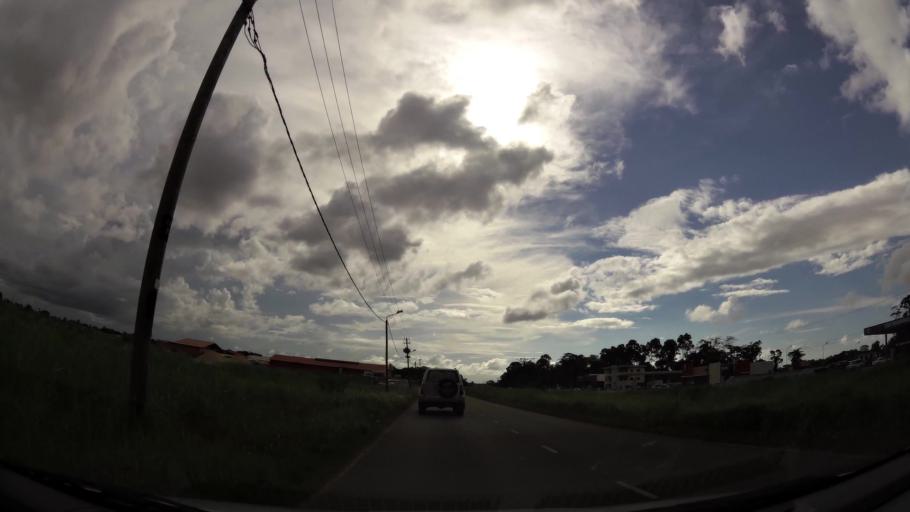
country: SR
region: Paramaribo
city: Paramaribo
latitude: 5.8564
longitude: -55.1690
